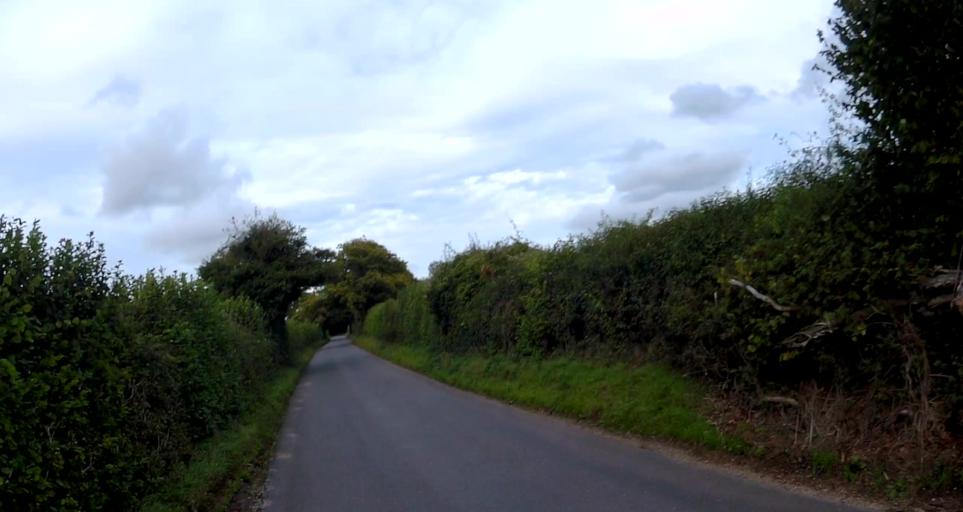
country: GB
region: England
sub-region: Hampshire
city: Four Marks
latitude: 51.1018
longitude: -1.1401
